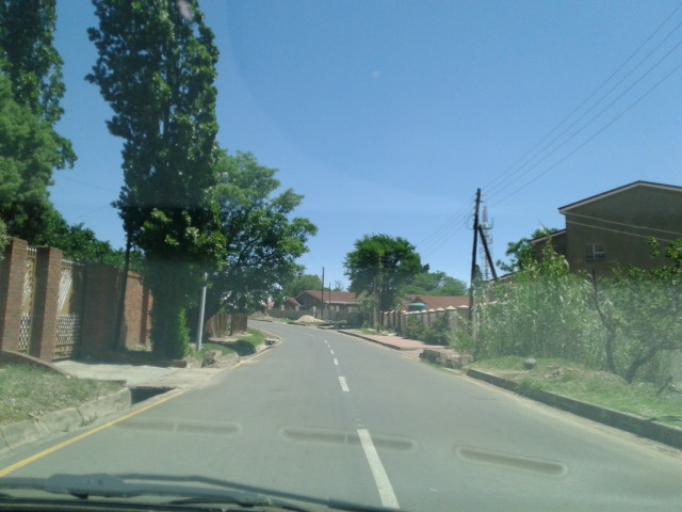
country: LS
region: Maseru
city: Maseru
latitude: -29.3047
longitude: 27.4734
